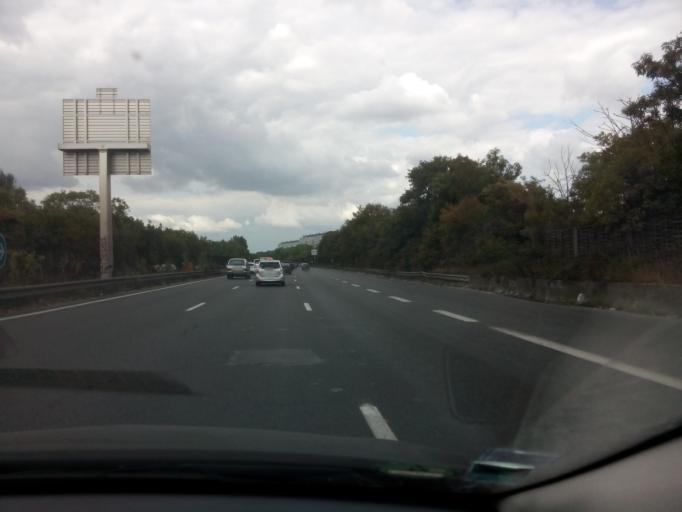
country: FR
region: Ile-de-France
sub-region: Departement de Seine-Saint-Denis
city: Bondy
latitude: 48.9081
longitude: 2.4734
